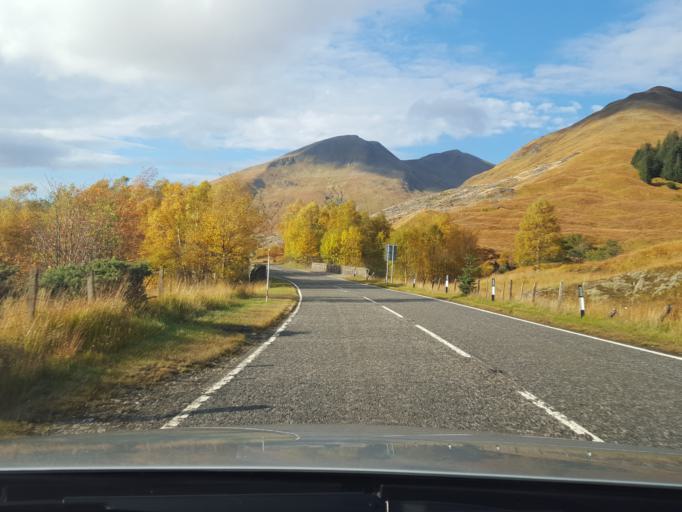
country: GB
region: Scotland
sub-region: Highland
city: Fort William
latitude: 57.1599
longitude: -5.1581
